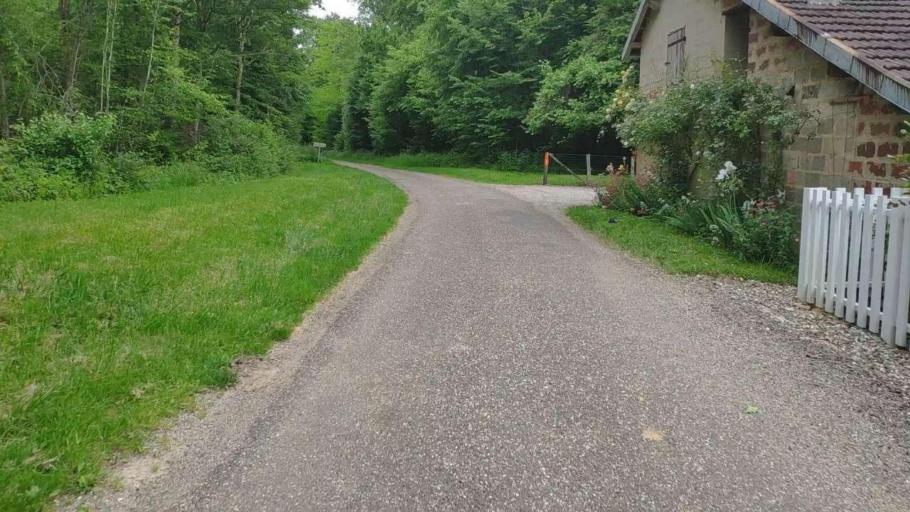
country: FR
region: Franche-Comte
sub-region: Departement du Jura
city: Bletterans
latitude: 46.7927
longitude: 5.5411
